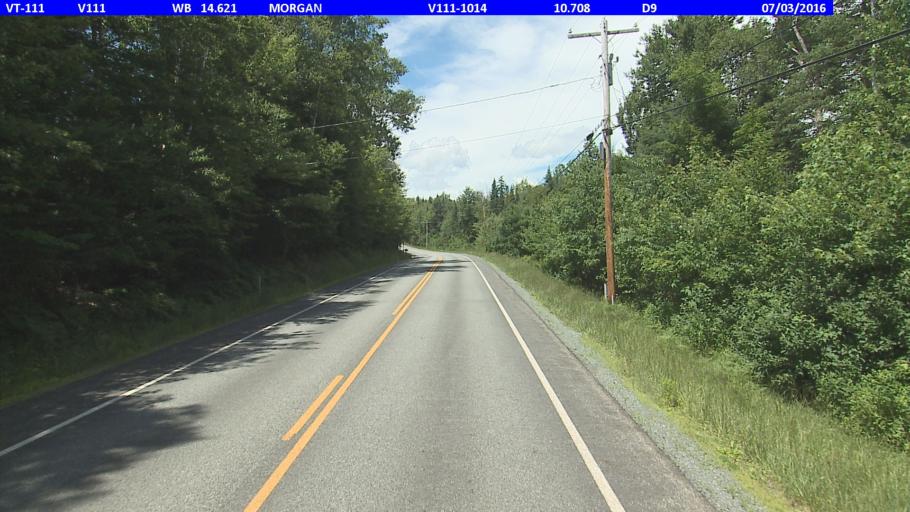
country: US
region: Vermont
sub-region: Orleans County
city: Newport
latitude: 44.8506
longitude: -71.9143
